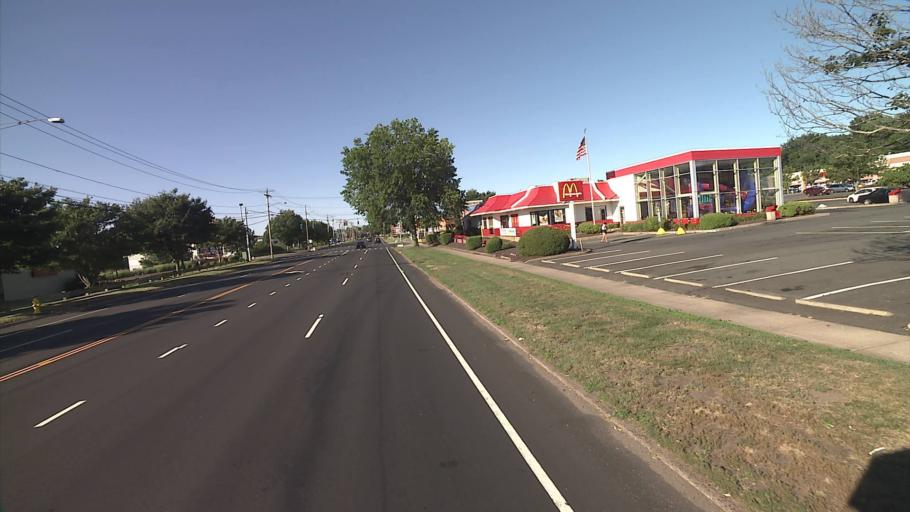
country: US
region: Connecticut
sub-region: New Haven County
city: Hamden
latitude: 41.3735
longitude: -72.9166
